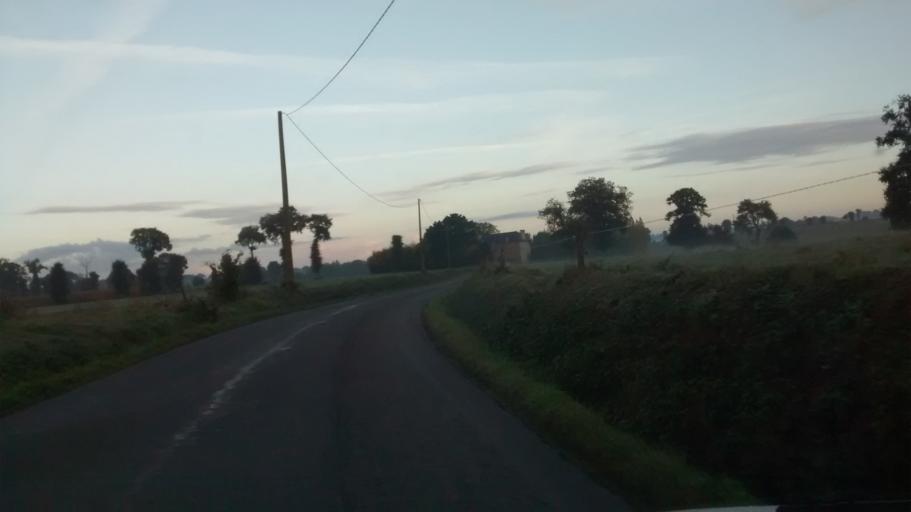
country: FR
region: Brittany
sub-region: Departement d'Ille-et-Vilaine
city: Betton
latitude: 48.1859
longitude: -1.6568
